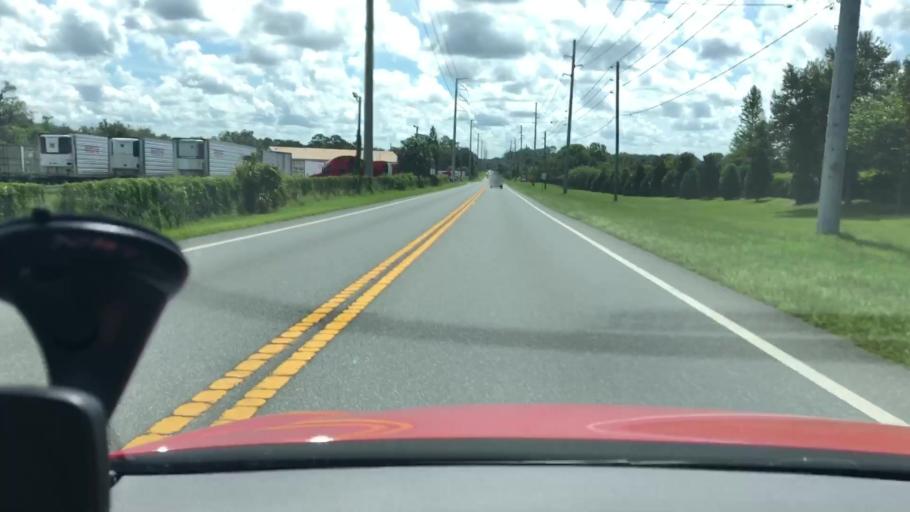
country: US
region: Florida
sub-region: Lake County
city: Eustis
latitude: 28.8813
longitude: -81.7190
